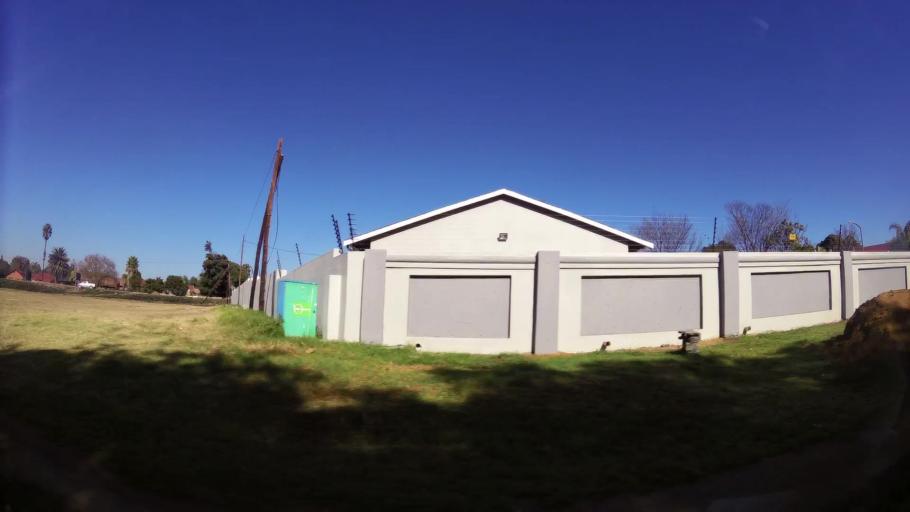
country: ZA
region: Mpumalanga
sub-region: Nkangala District Municipality
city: Witbank
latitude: -25.8904
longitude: 29.2369
